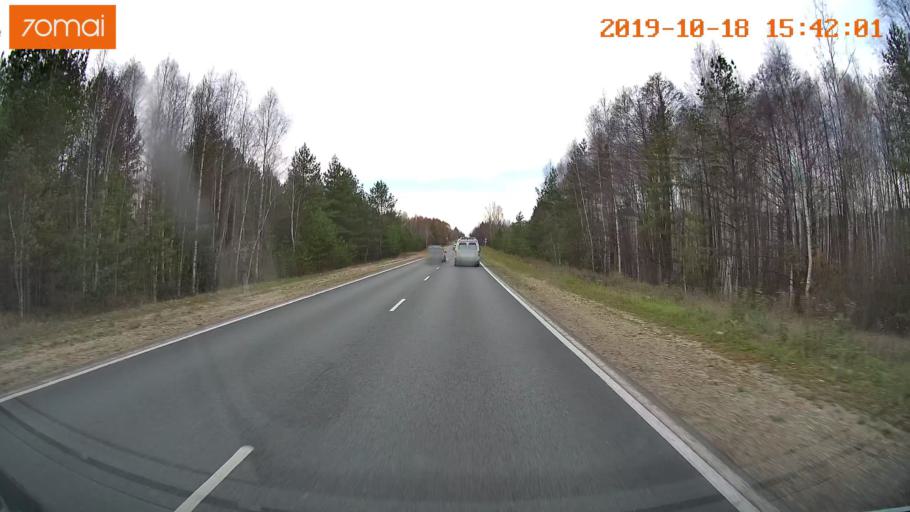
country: RU
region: Vladimir
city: Golovino
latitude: 55.9515
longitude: 40.5740
